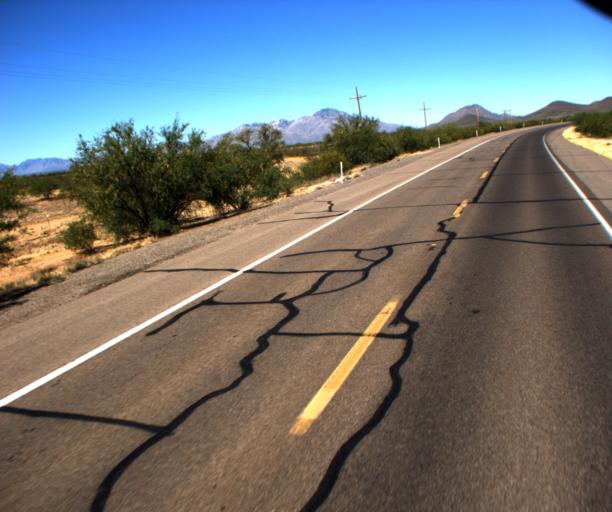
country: US
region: Arizona
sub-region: Pima County
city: Three Points
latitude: 32.0751
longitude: -111.3323
